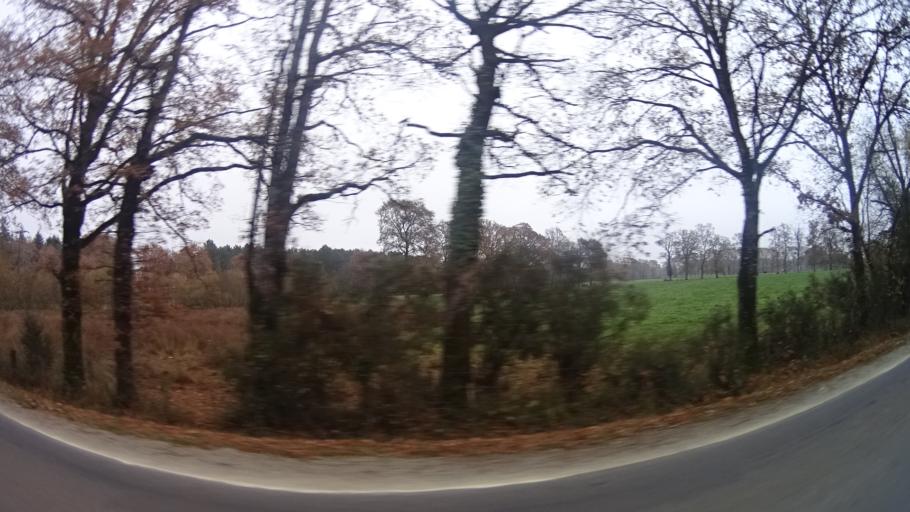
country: FR
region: Brittany
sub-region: Departement d'Ille-et-Vilaine
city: Bains-sur-Oust
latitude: 47.6970
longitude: -2.0565
